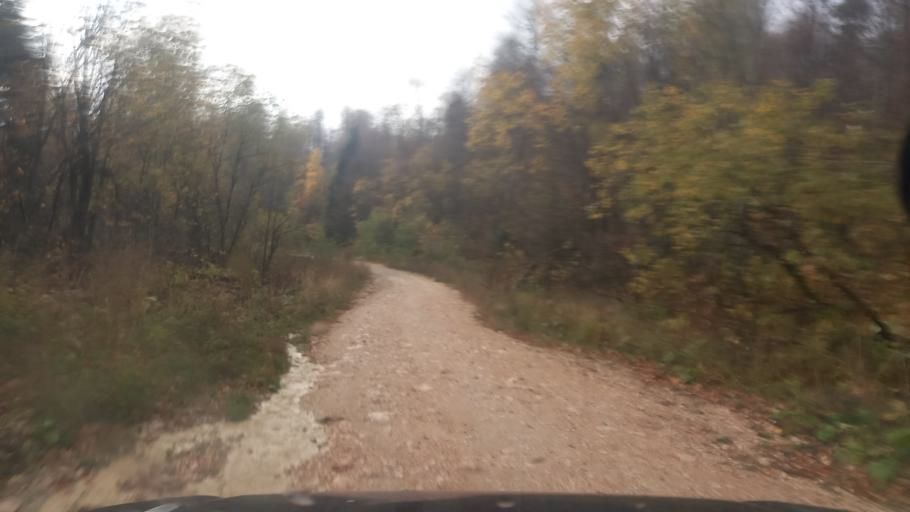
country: RU
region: Krasnodarskiy
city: Gornoye Loo
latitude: 44.0034
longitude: 39.8459
